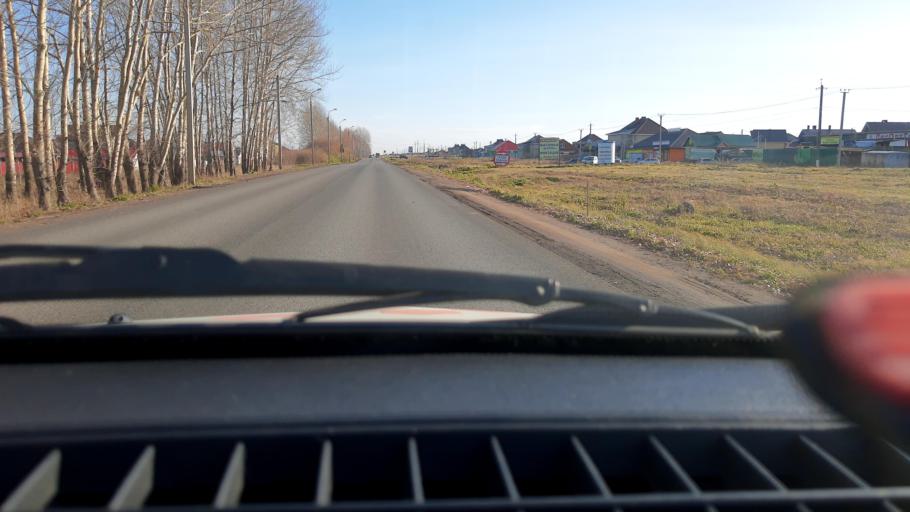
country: RU
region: Bashkortostan
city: Kabakovo
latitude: 54.6165
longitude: 56.1294
